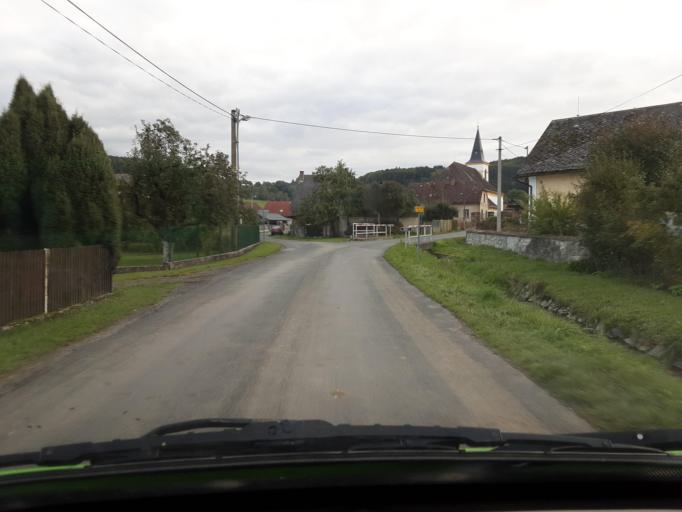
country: CZ
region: Plzensky
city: Janovice nad Uhlavou
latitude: 49.3886
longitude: 13.1527
